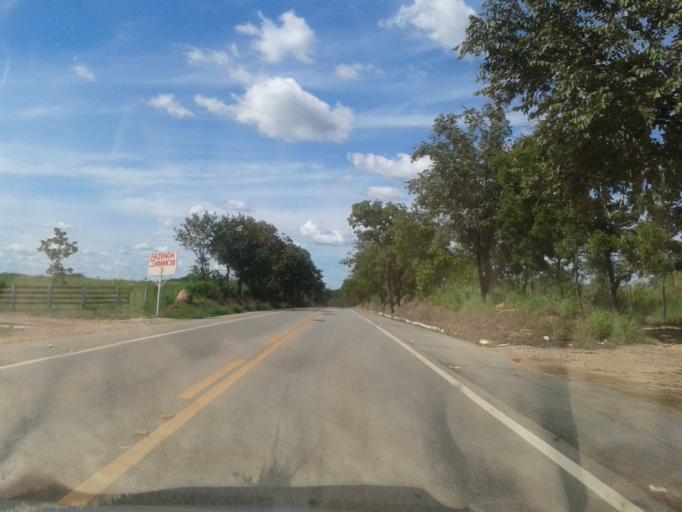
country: BR
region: Goias
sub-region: Itapuranga
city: Itapuranga
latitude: -15.4161
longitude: -50.3773
